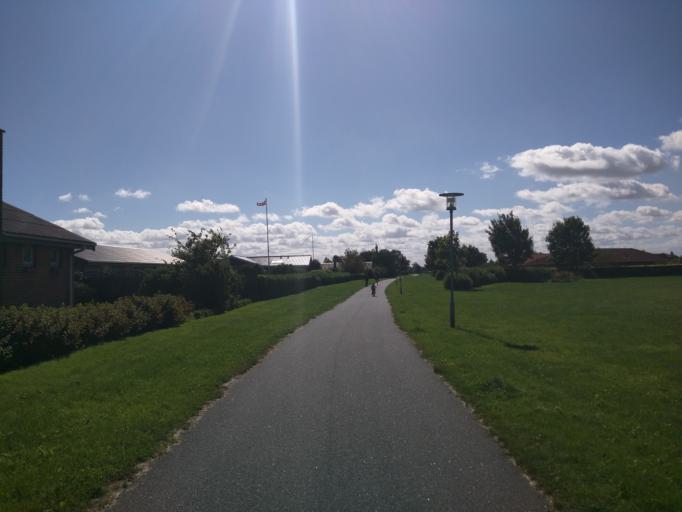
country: DK
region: Central Jutland
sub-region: Viborg Kommune
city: Viborg
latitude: 56.4683
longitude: 9.3841
